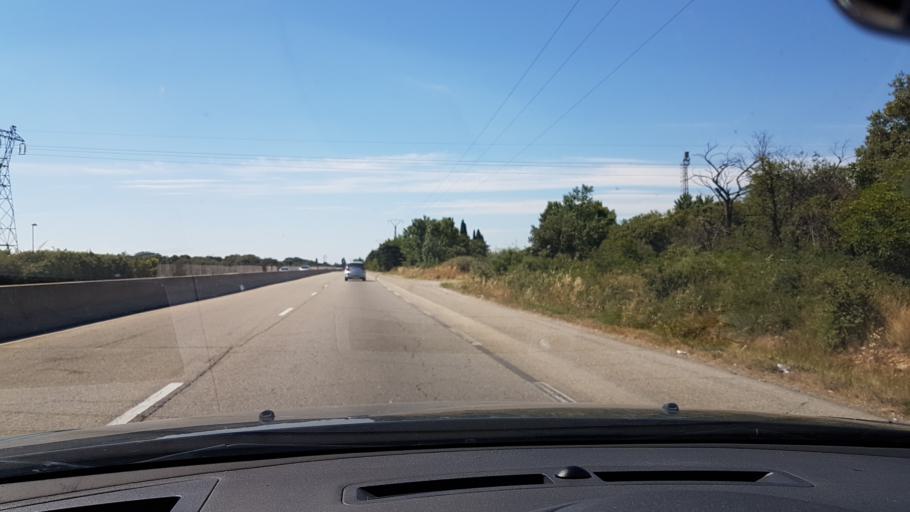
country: FR
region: Provence-Alpes-Cote d'Azur
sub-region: Departement des Bouches-du-Rhone
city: Fos-sur-Mer
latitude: 43.4638
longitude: 4.9171
